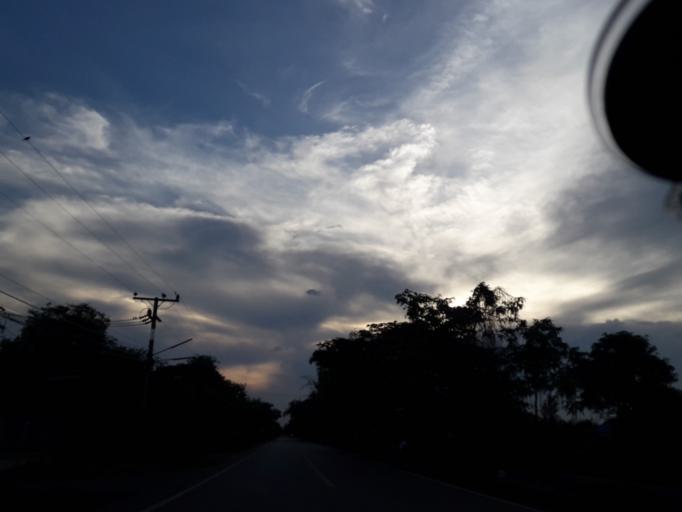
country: TH
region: Sara Buri
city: Nong Khae
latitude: 14.2721
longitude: 100.8837
